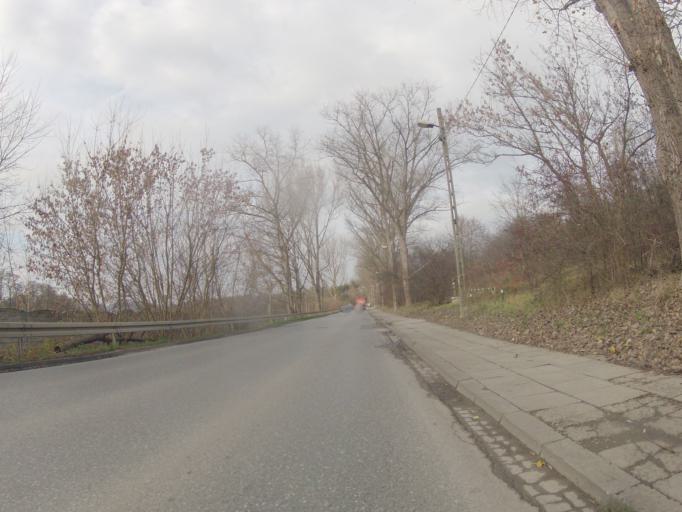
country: PL
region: Lesser Poland Voivodeship
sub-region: Powiat krakowski
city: Rzaska
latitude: 50.0881
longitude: 19.8401
